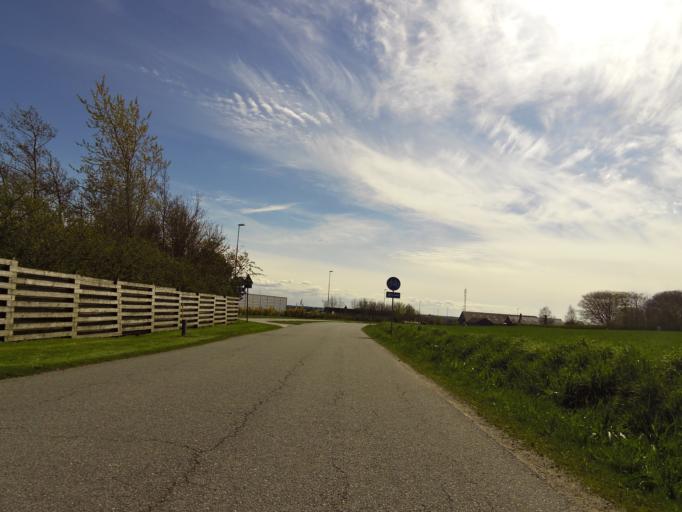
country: DK
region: Central Jutland
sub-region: Skive Kommune
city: Skive
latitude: 56.5719
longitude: 9.0004
